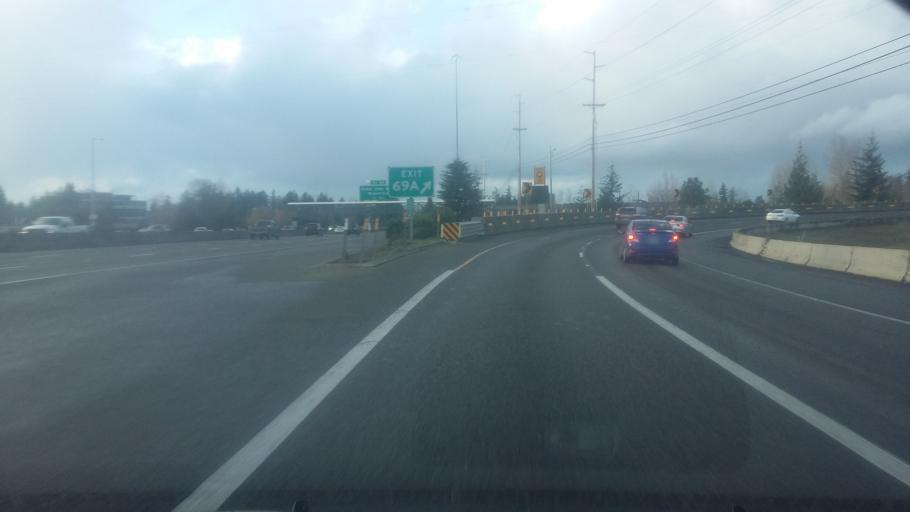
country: US
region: Oregon
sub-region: Washington County
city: West Haven
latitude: 45.5087
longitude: -122.7787
